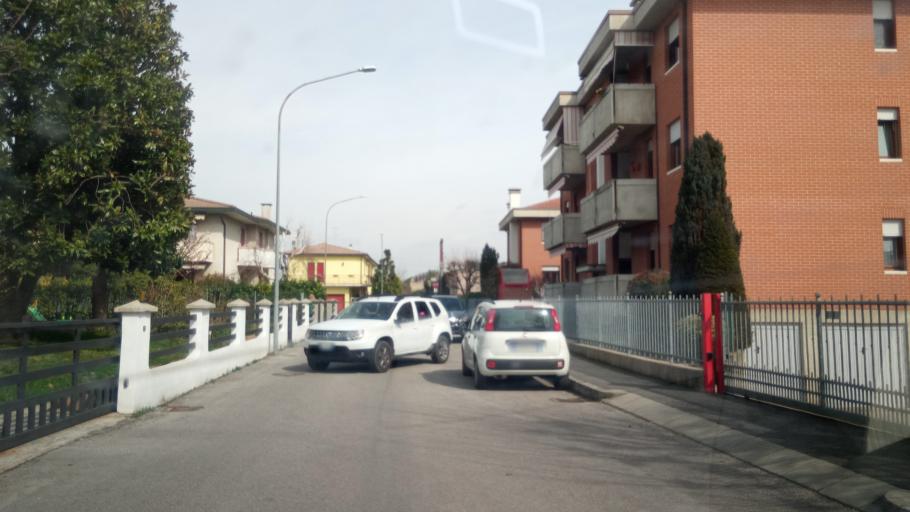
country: IT
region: Veneto
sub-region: Provincia di Padova
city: Vigodarzere
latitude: 45.4560
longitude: 11.8781
